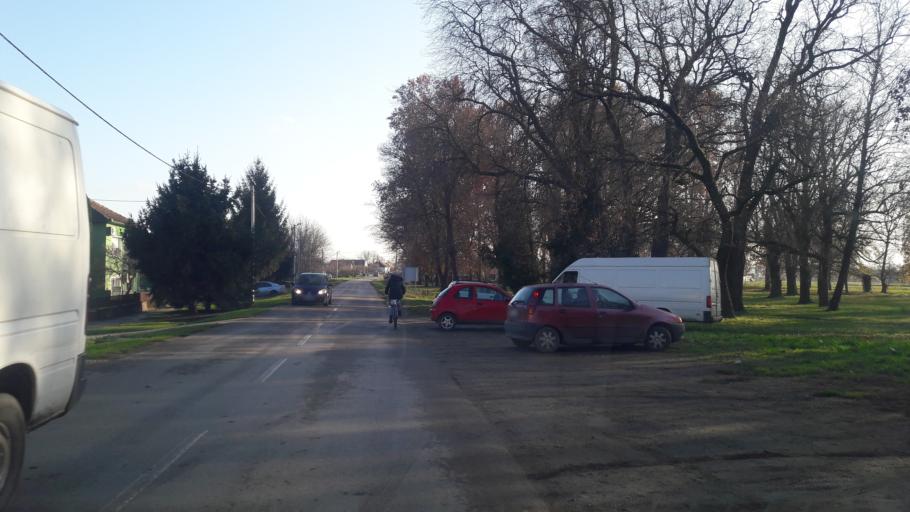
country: HR
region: Osjecko-Baranjska
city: Darda
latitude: 45.6220
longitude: 18.6876
